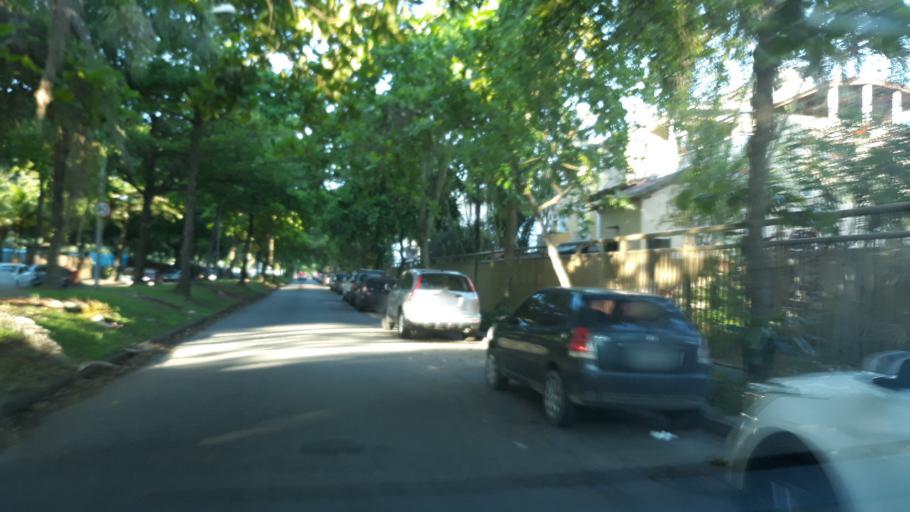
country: BR
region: Rio de Janeiro
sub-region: Rio De Janeiro
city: Rio de Janeiro
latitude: -23.0058
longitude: -43.3391
